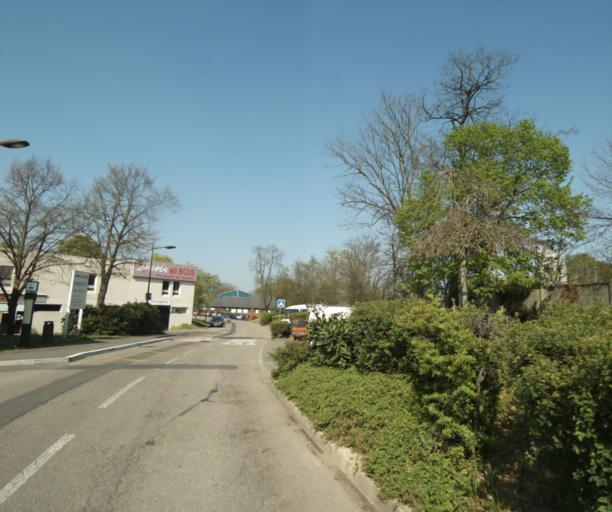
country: FR
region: Ile-de-France
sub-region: Departement des Hauts-de-Seine
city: Sevres
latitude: 48.8140
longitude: 2.2139
